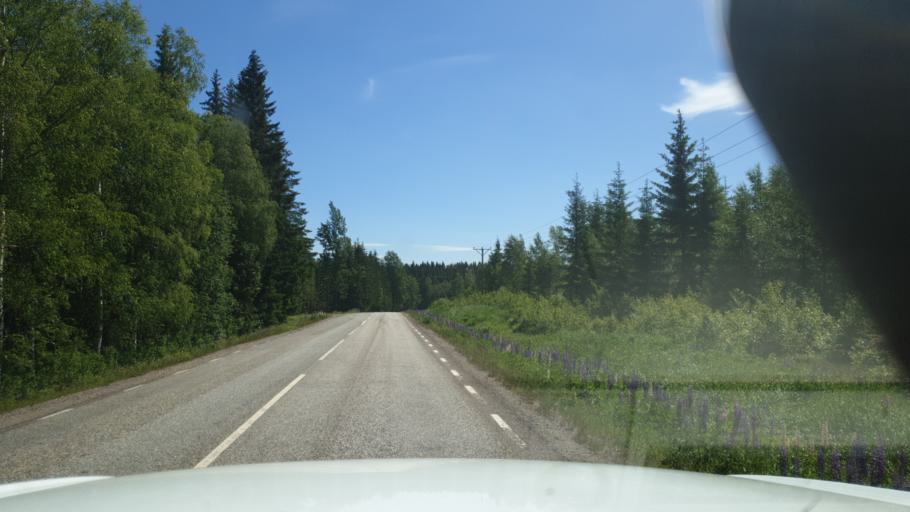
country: SE
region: Vaermland
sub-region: Arjangs Kommun
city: Arjaeng
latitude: 59.5782
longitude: 12.2456
